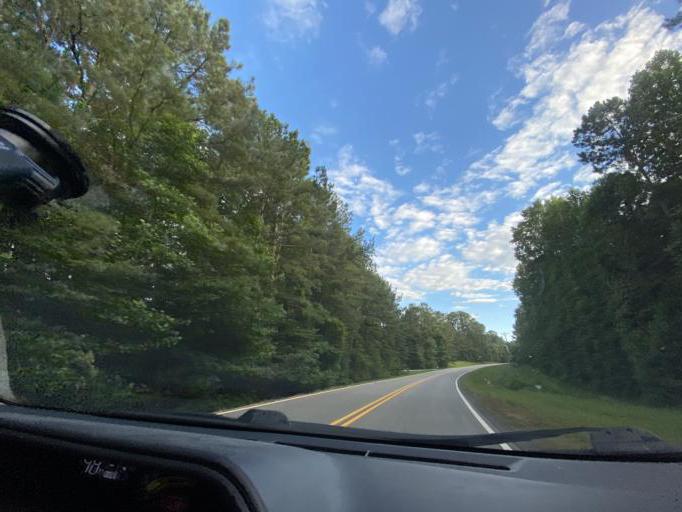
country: US
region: Georgia
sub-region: Fayette County
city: Peachtree City
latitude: 33.4251
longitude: -84.6502
